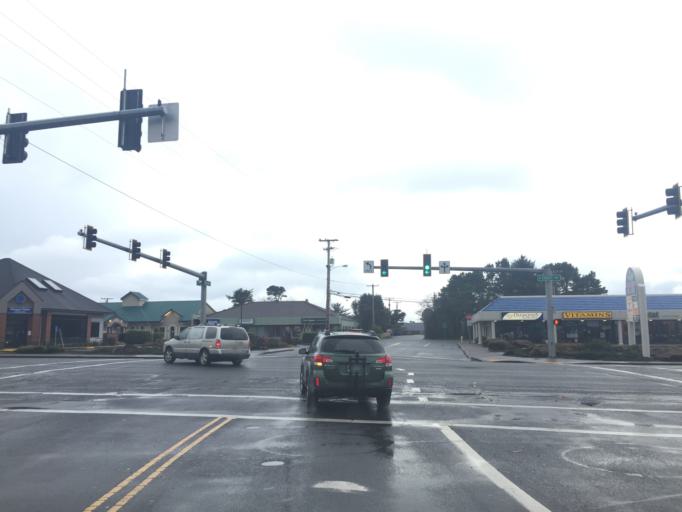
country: US
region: Oregon
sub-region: Lincoln County
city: Newport
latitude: 44.6516
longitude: -124.0527
